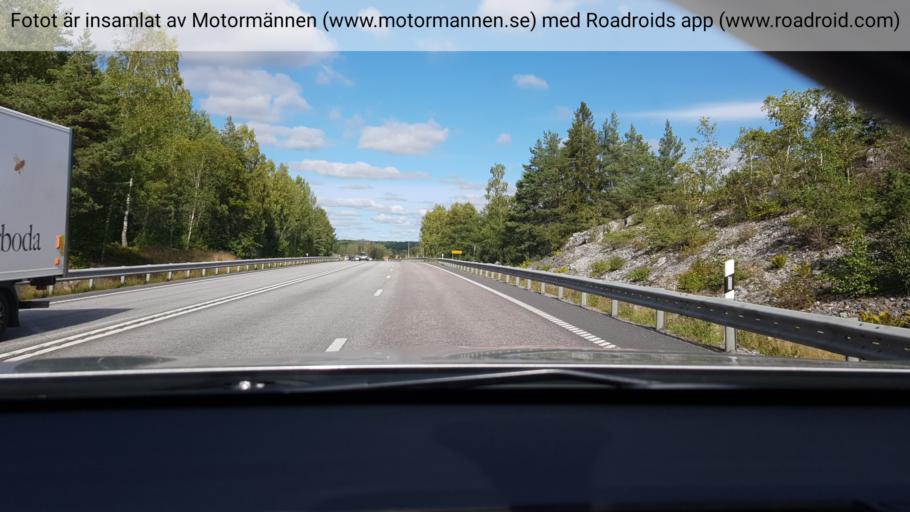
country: SE
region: Stockholm
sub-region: Osterakers Kommun
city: Akersberga
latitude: 59.4397
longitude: 18.2218
